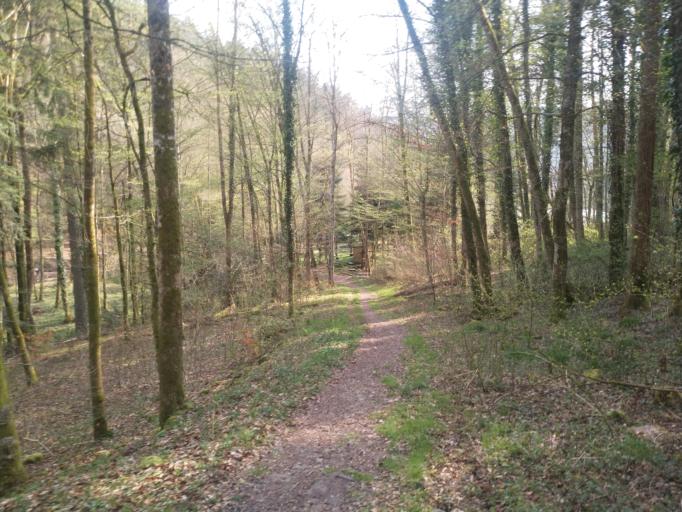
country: DE
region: Baden-Wuerttemberg
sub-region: Karlsruhe Region
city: Bad Liebenzell
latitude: 48.8031
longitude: 8.7368
